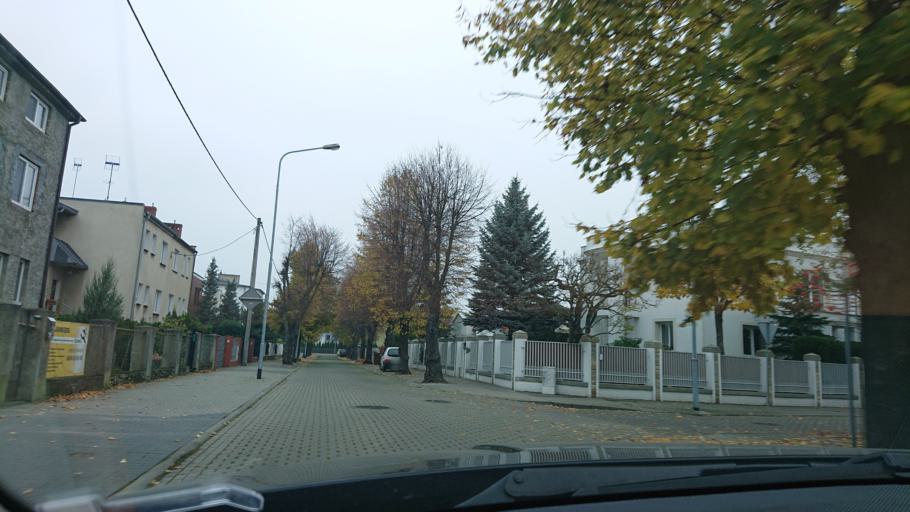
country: PL
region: Greater Poland Voivodeship
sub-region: Powiat gnieznienski
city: Gniezno
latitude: 52.5335
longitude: 17.6213
